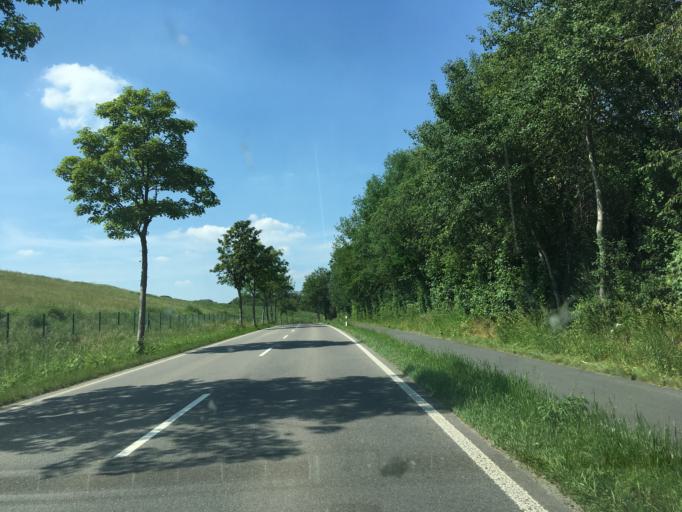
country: DE
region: North Rhine-Westphalia
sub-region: Regierungsbezirk Munster
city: Borken
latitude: 51.8352
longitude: 6.7833
